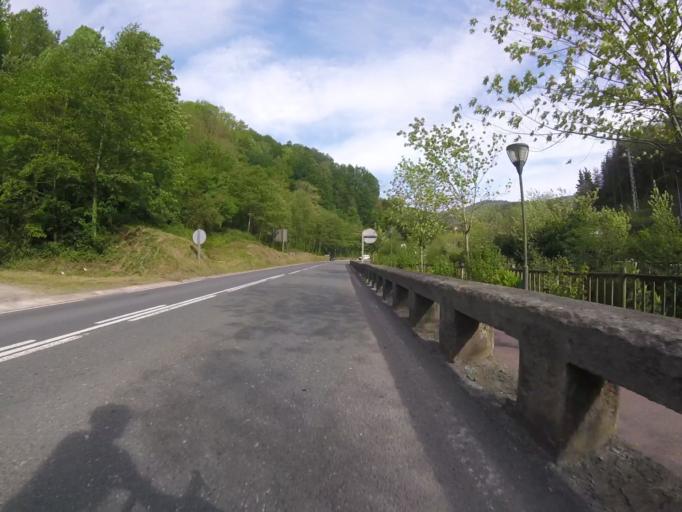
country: ES
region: Basque Country
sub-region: Provincia de Guipuzcoa
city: Urretxu
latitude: 43.1043
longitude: -2.3173
